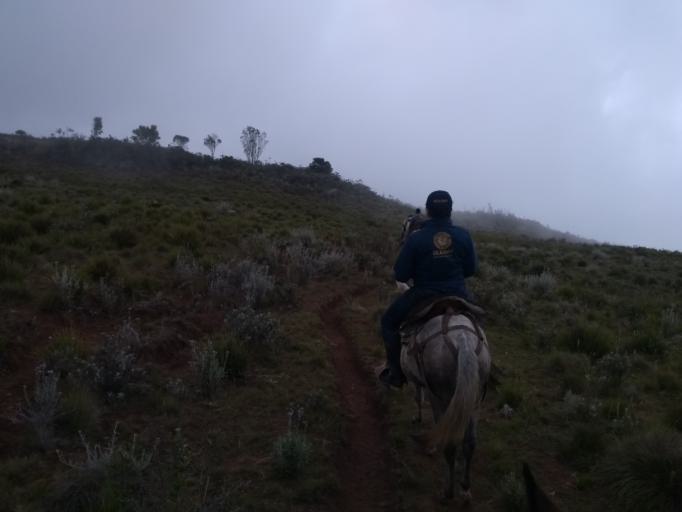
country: CO
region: Cesar
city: Manaure Balcon del Cesar
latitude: 10.2096
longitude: -73.0089
